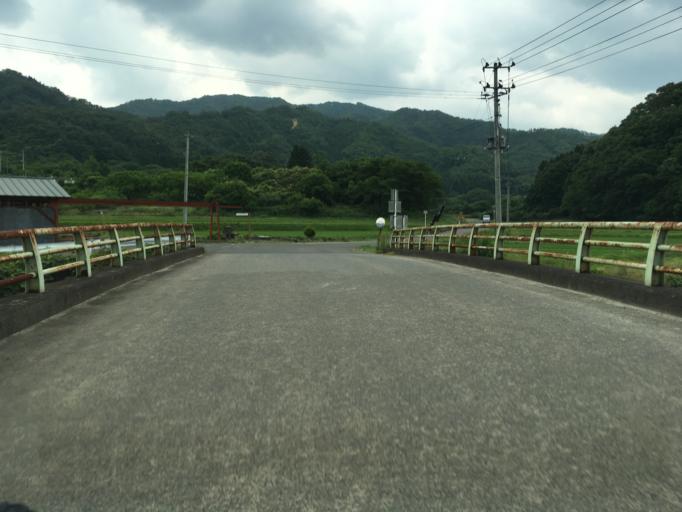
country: JP
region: Fukushima
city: Hobaramachi
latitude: 37.7126
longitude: 140.6043
